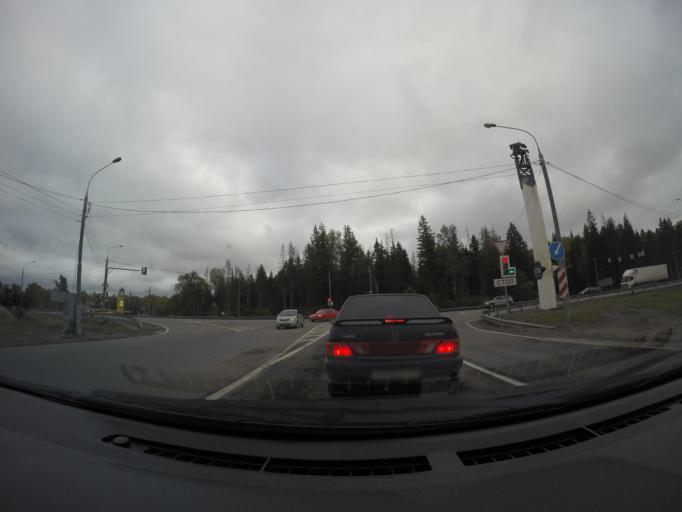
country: RU
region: Moskovskaya
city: Dorokhovo
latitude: 55.5390
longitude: 36.3986
